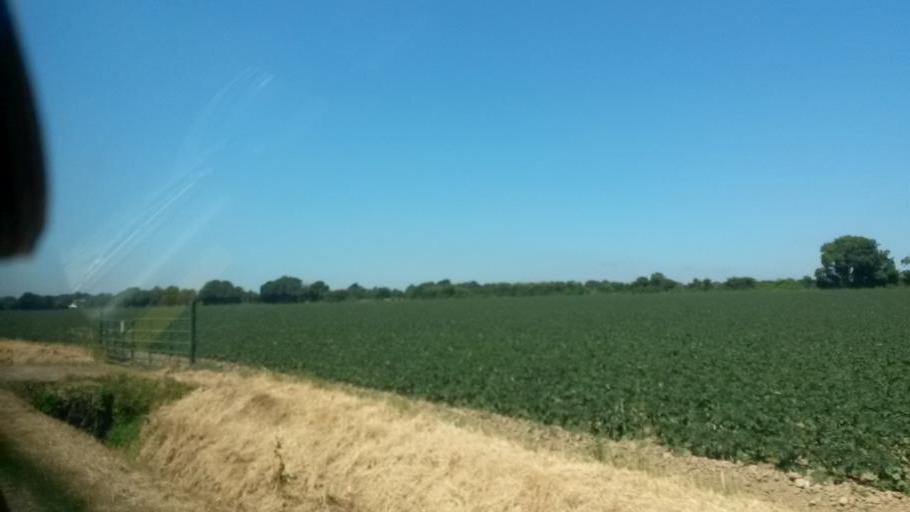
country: IE
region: Leinster
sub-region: Fingal County
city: Swords
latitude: 53.5185
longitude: -6.2573
